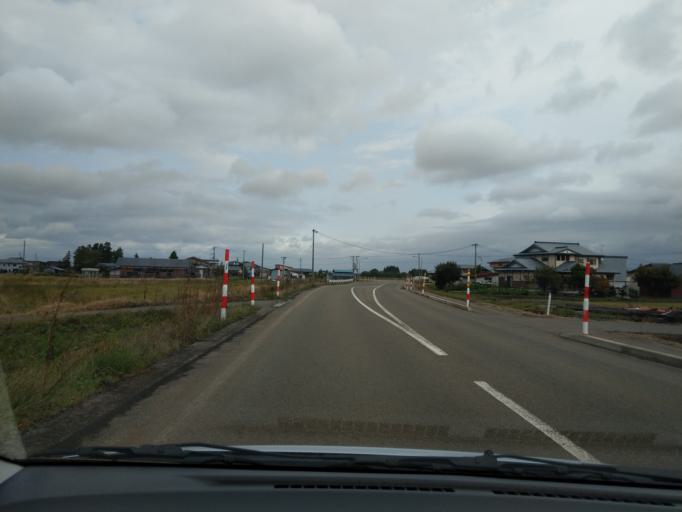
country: JP
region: Akita
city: Omagari
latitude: 39.3802
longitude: 140.4858
